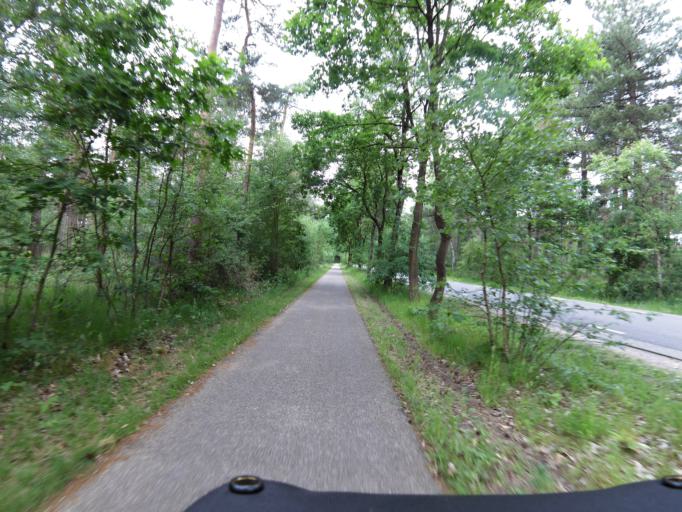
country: NL
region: North Brabant
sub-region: Gemeente Hilvarenbeek
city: Hilvarenbeek
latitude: 51.4110
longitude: 5.1133
